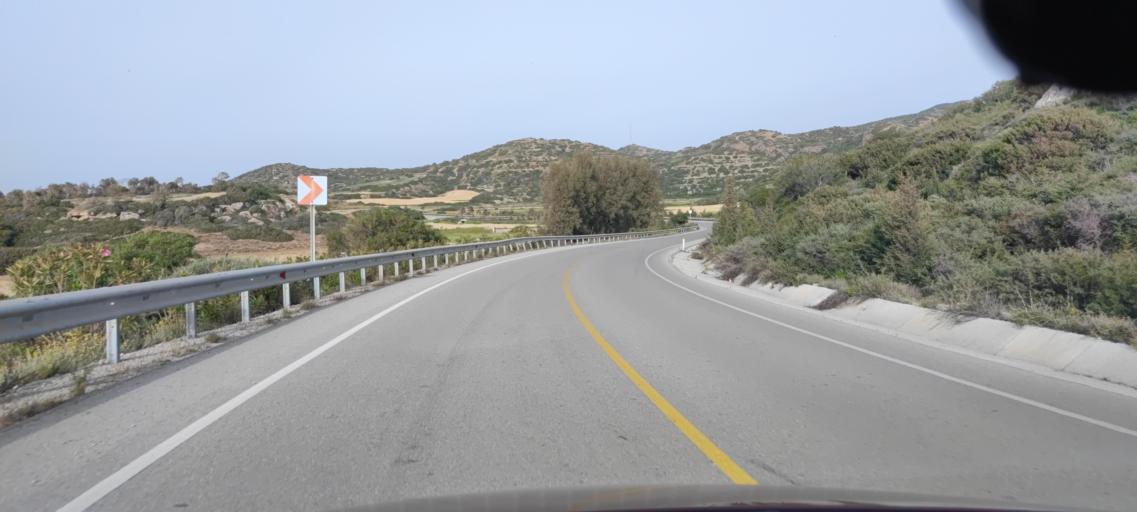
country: CY
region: Ammochostos
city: Leonarisso
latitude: 35.4861
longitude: 34.0735
